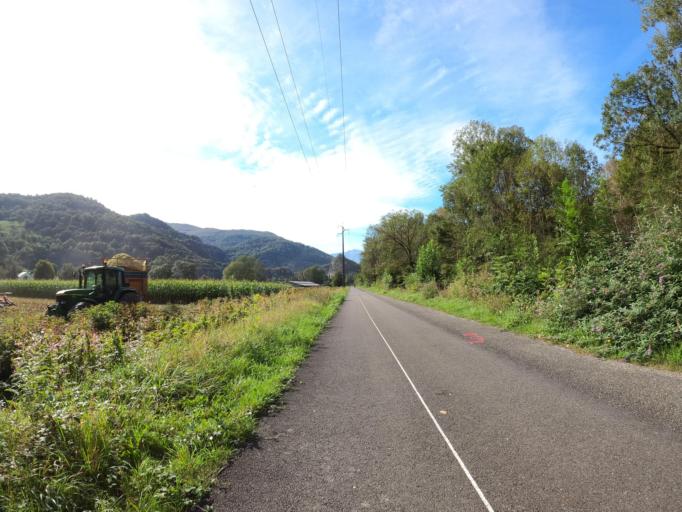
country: FR
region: Midi-Pyrenees
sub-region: Departement des Hautes-Pyrenees
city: Lourdes
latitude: 43.0553
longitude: -0.0439
